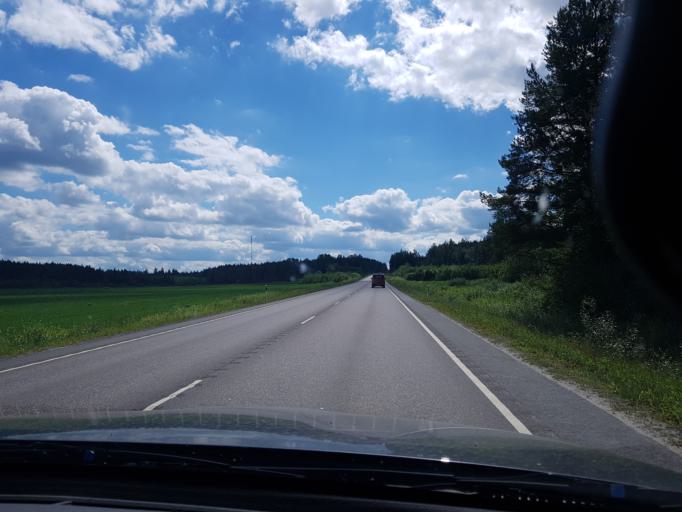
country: FI
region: Haeme
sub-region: Haemeenlinna
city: Parola
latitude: 61.0963
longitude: 24.4046
